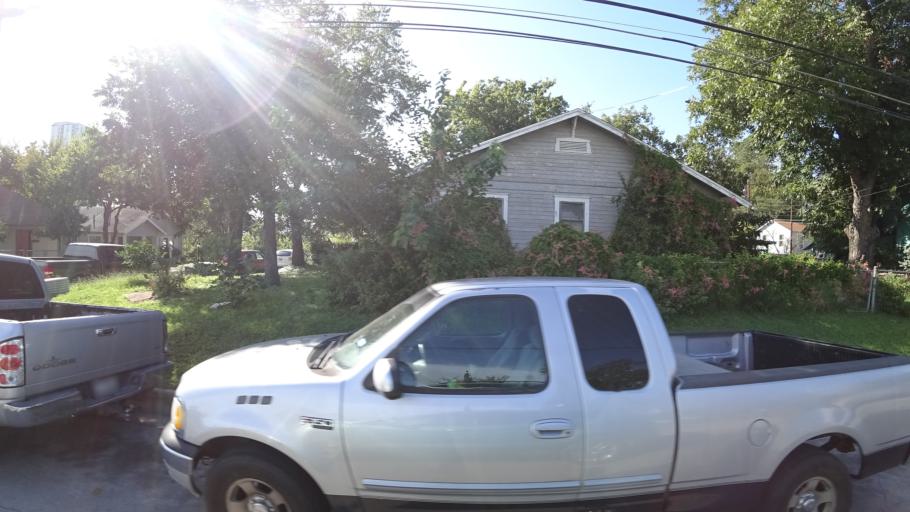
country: US
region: Texas
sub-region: Travis County
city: Austin
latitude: 30.2581
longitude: -97.7357
